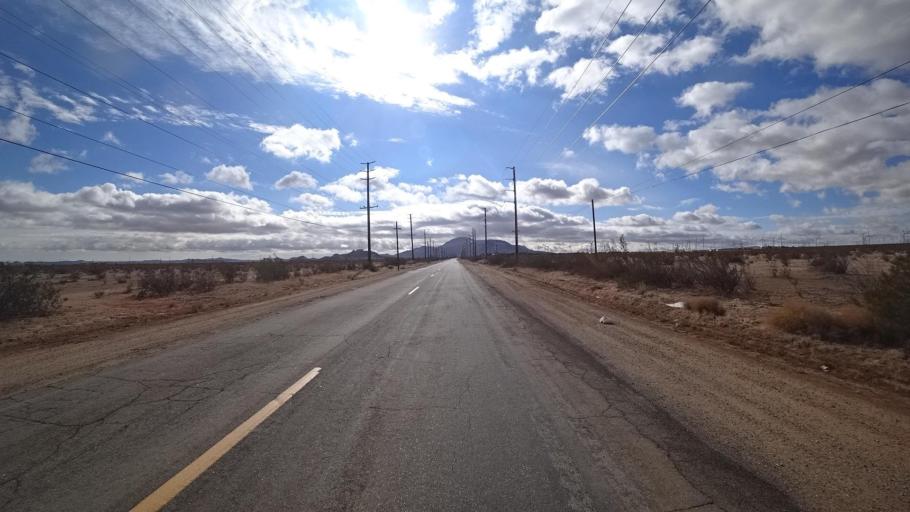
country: US
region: California
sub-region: Kern County
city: Mojave
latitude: 35.0434
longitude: -118.1854
